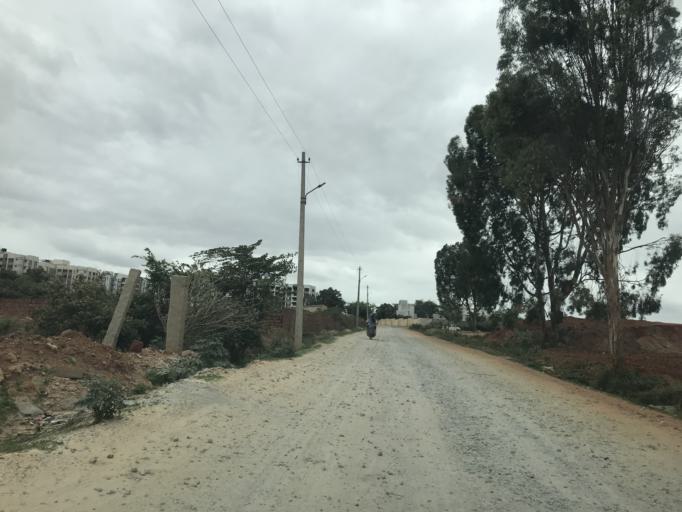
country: IN
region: Karnataka
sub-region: Bangalore Rural
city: Devanhalli
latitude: 13.2136
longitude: 77.6574
